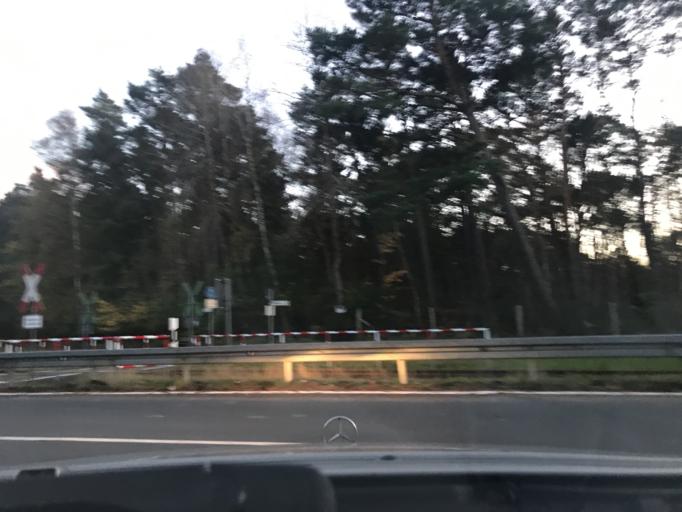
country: DE
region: Mecklenburg-Vorpommern
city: Karlshagen
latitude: 54.1450
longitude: 13.8095
